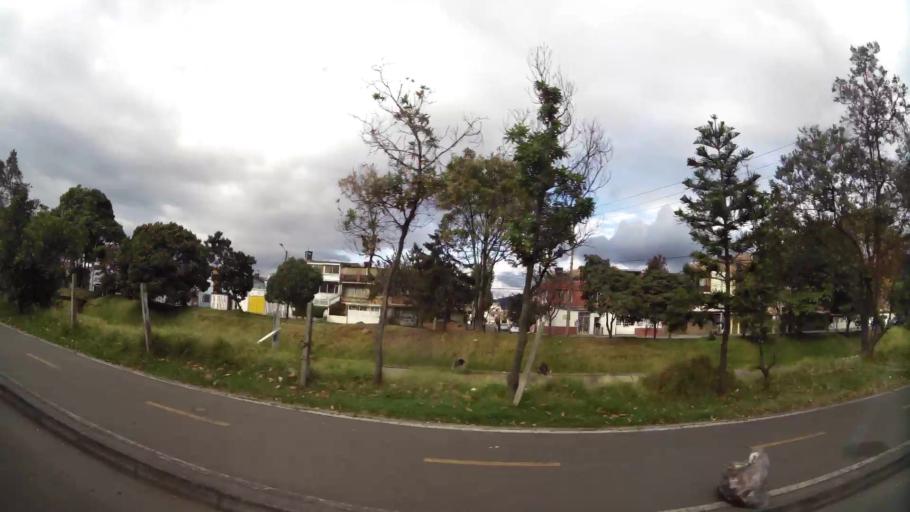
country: CO
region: Bogota D.C.
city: Bogota
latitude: 4.6037
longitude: -74.1181
